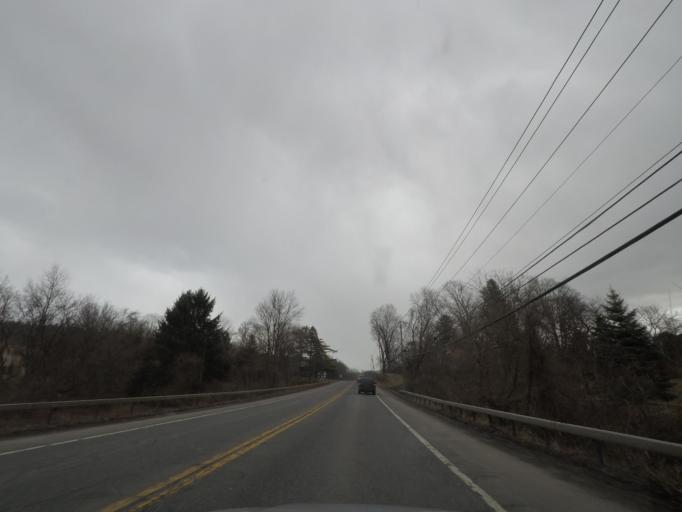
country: US
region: New York
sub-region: Onondaga County
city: Fayetteville
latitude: 43.0335
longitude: -75.9830
